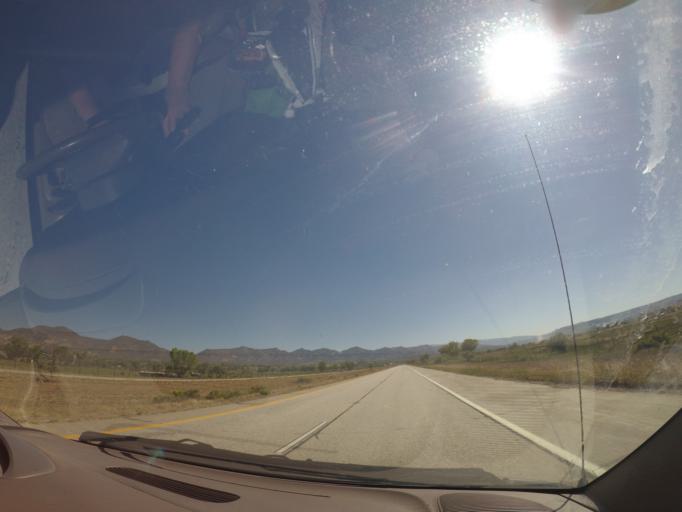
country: US
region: Colorado
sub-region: Garfield County
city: Silt
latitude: 39.5359
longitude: -107.6859
